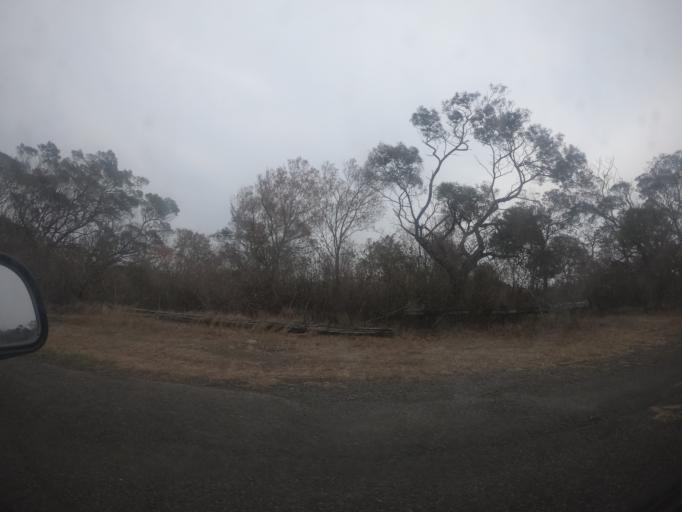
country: AU
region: New South Wales
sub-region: Shellharbour
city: Croom
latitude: -34.6134
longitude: 150.8536
